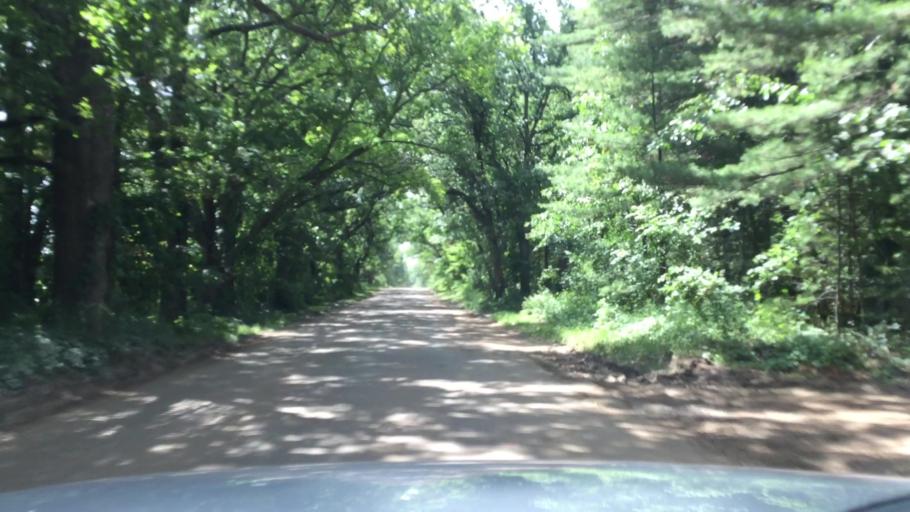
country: US
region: Michigan
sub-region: Ionia County
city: Belding
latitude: 43.1408
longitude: -85.2135
